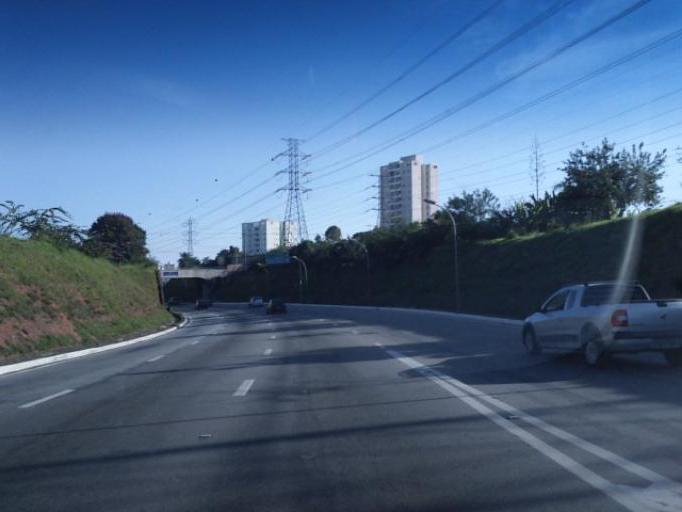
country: BR
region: Sao Paulo
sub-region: Sao Jose Dos Campos
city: Sao Jose dos Campos
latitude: -23.2064
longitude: -45.8924
